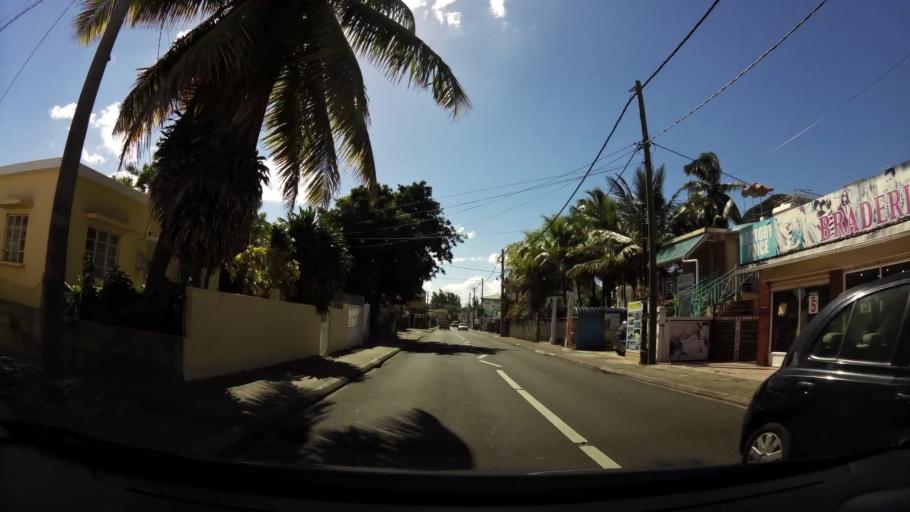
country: MU
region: Black River
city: Flic en Flac
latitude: -20.2777
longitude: 57.3691
